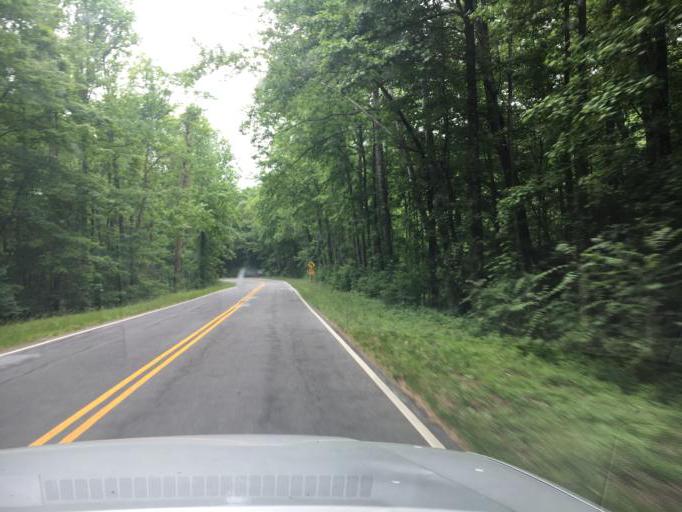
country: US
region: South Carolina
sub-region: Greenville County
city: Tigerville
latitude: 35.1515
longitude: -82.4194
